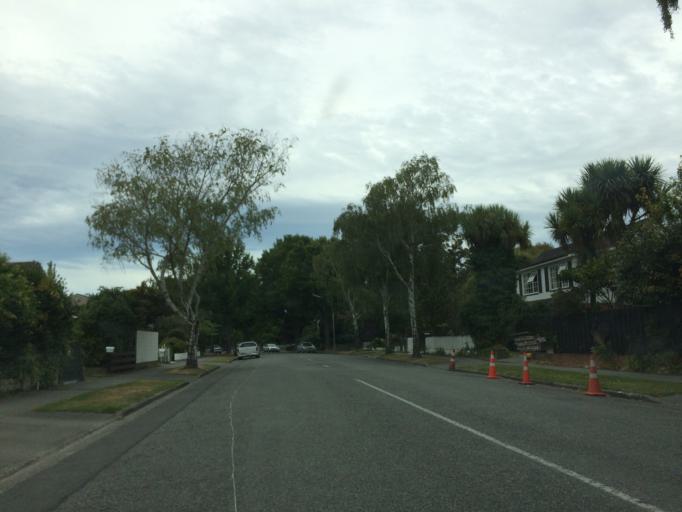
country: NZ
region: Canterbury
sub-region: Christchurch City
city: Christchurch
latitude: -43.5221
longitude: 172.5614
